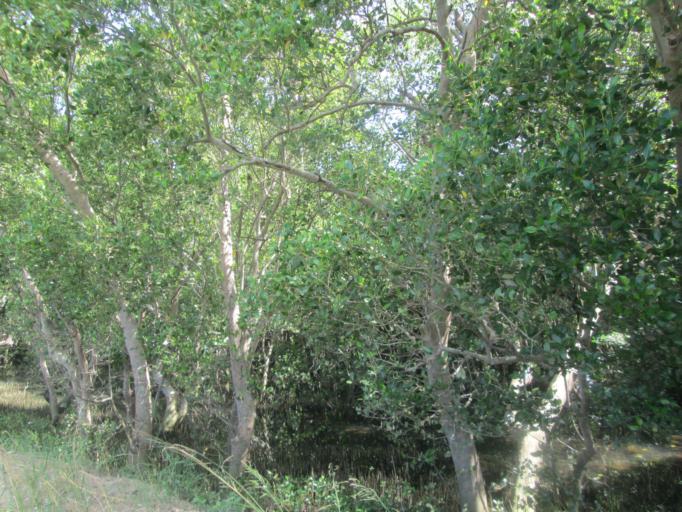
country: PH
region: Ilocos
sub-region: Province of Pangasinan
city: Pangapisan
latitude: 16.2430
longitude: 119.9296
